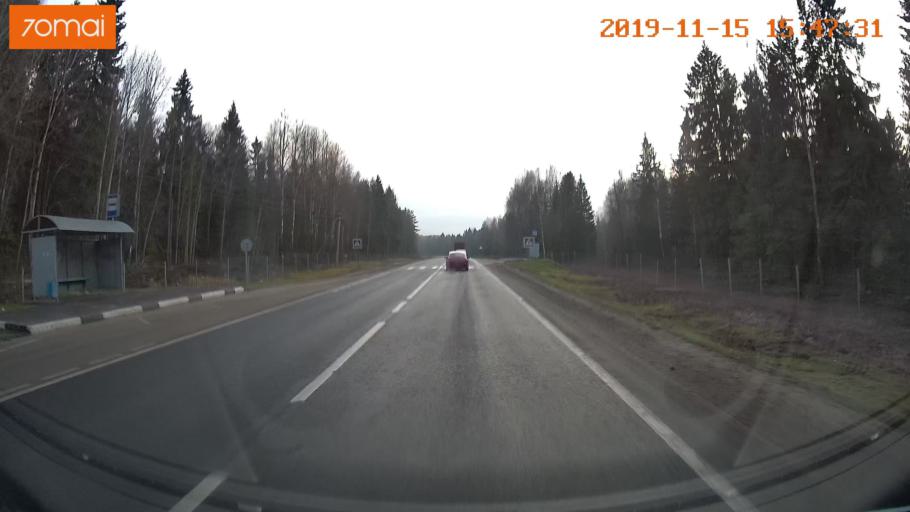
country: RU
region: Jaroslavl
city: Danilov
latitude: 57.9374
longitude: 40.0091
